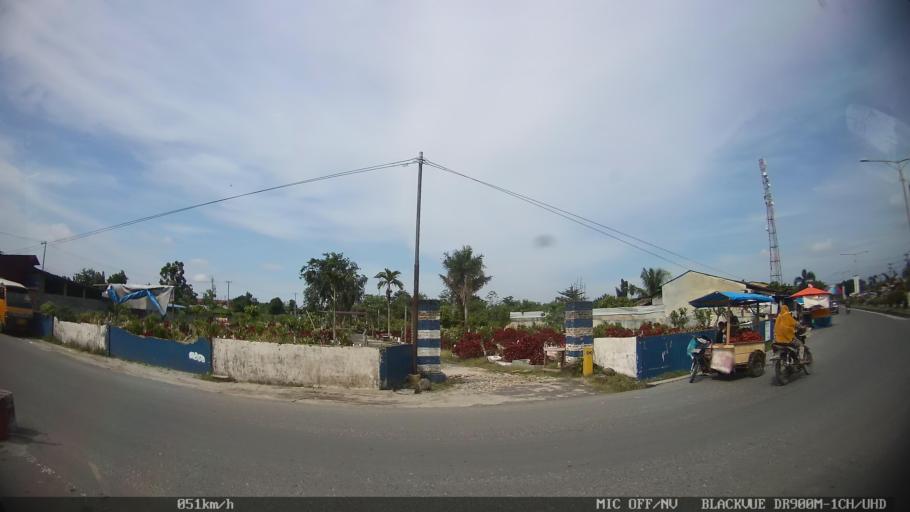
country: ID
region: North Sumatra
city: Percut
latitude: 3.6127
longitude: 98.8037
